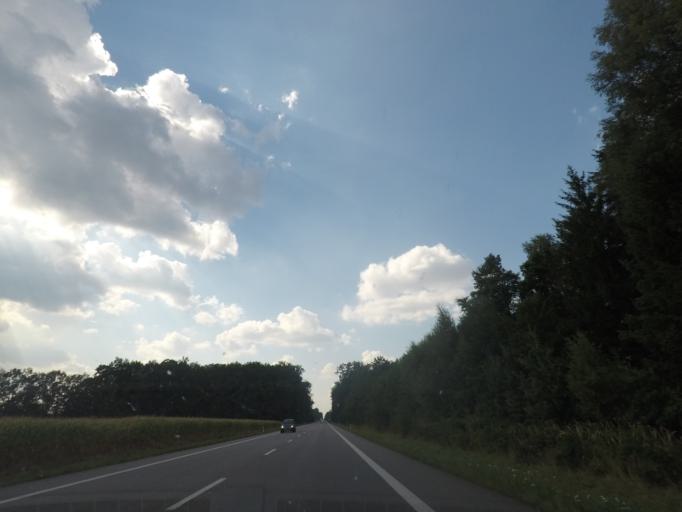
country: CZ
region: Kralovehradecky
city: Trebechovice pod Orebem
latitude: 50.1758
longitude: 16.0304
